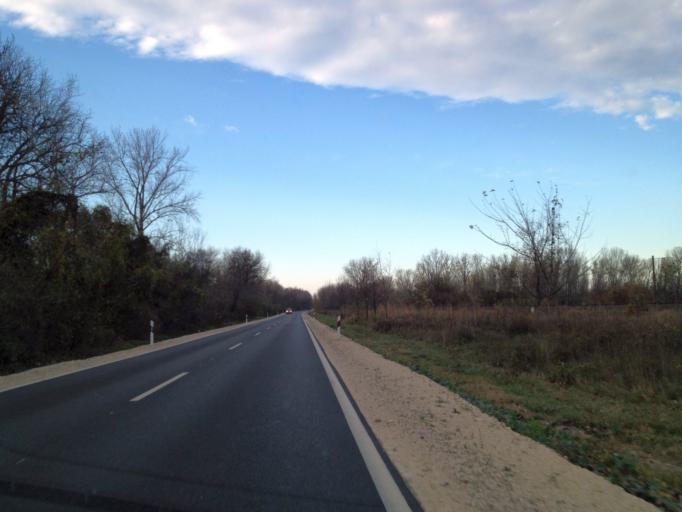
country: HU
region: Gyor-Moson-Sopron
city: Nyul
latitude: 47.6075
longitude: 17.6855
